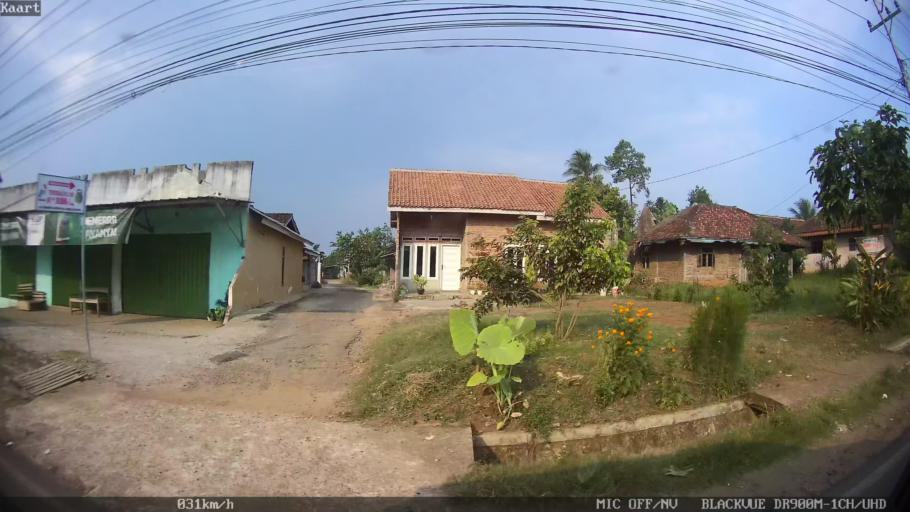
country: ID
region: Lampung
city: Natar
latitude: -5.3703
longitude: 105.1922
